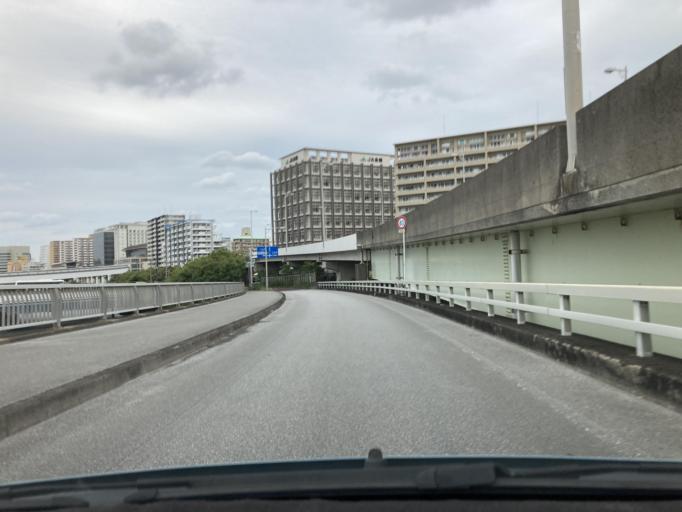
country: JP
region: Okinawa
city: Naha-shi
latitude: 26.2007
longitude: 127.6800
